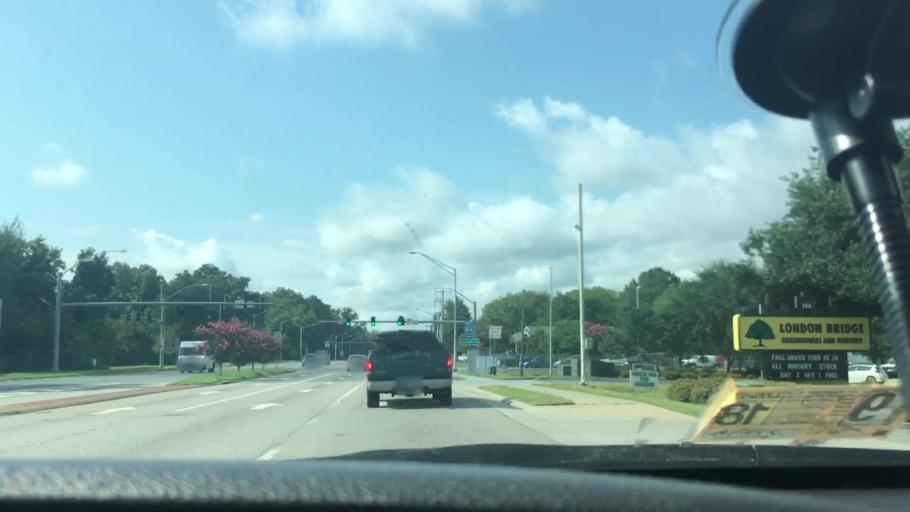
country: US
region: Virginia
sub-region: City of Virginia Beach
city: Virginia Beach
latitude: 36.8394
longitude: -76.0493
